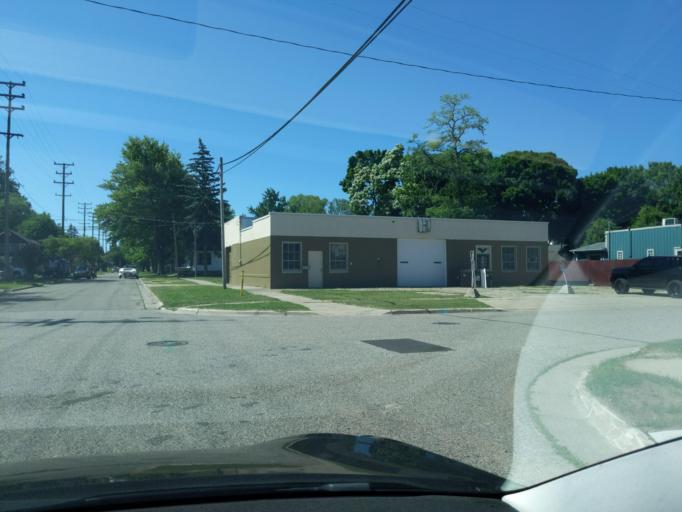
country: US
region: Michigan
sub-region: Muskegon County
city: Muskegon
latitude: 43.2268
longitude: -86.2666
